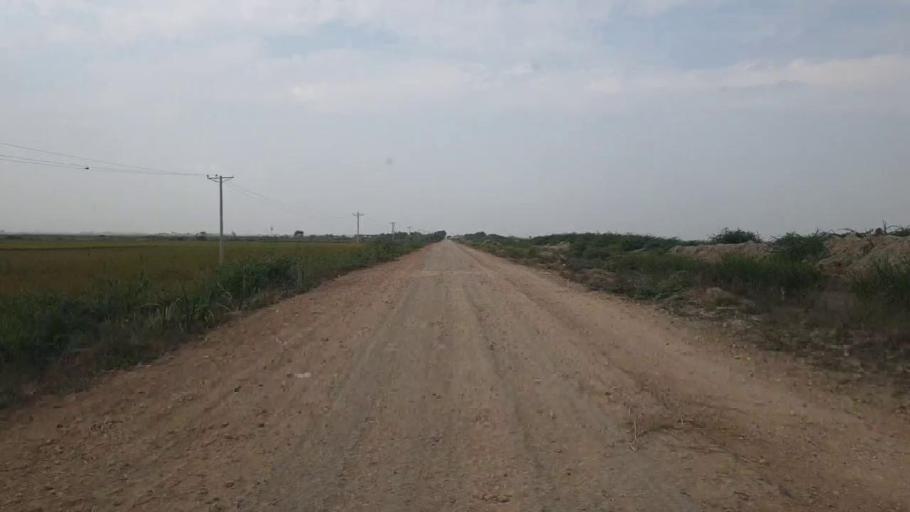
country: PK
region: Sindh
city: Kario
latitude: 24.6175
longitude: 68.5855
